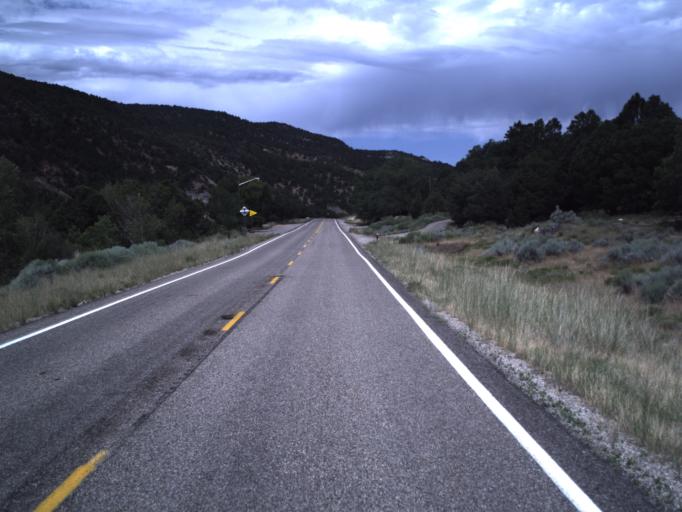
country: US
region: Utah
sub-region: Iron County
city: Cedar City
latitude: 37.6521
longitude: -112.9823
